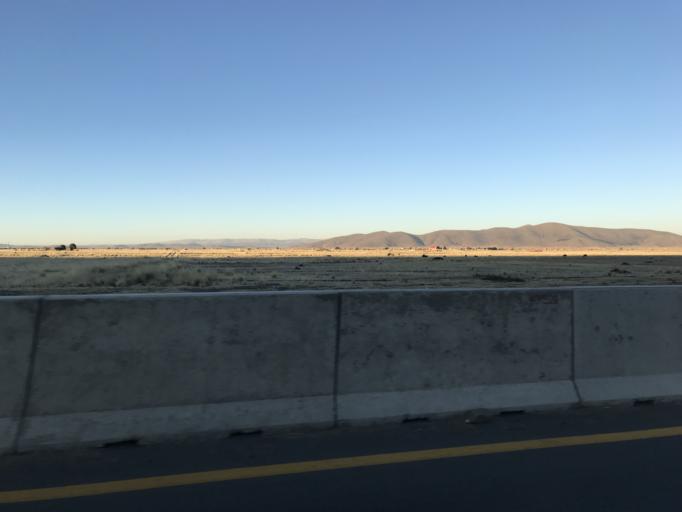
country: BO
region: La Paz
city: Batallas
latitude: -16.2990
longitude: -68.5140
